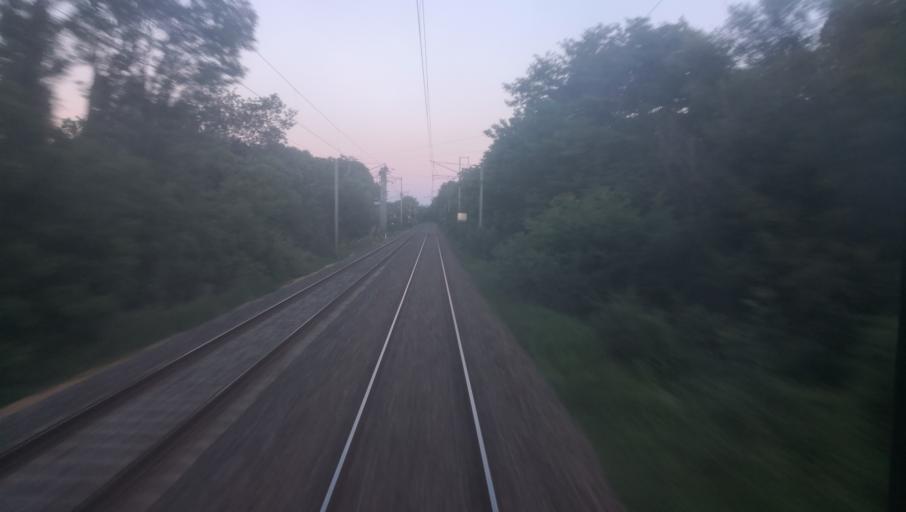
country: FR
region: Bourgogne
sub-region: Departement de la Nievre
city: Neuvy-sur-Loire
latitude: 47.5115
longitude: 2.8916
